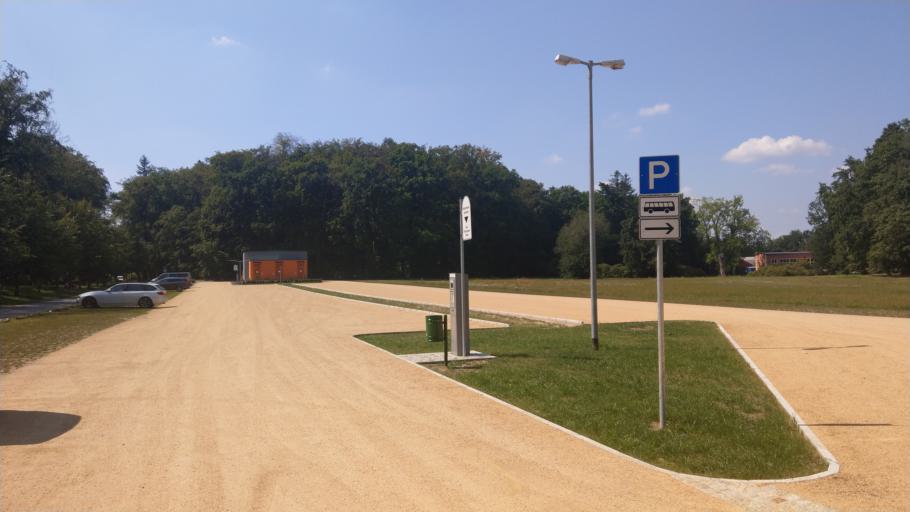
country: DE
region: Saxony
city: Gablenz
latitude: 51.5374
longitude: 14.6375
